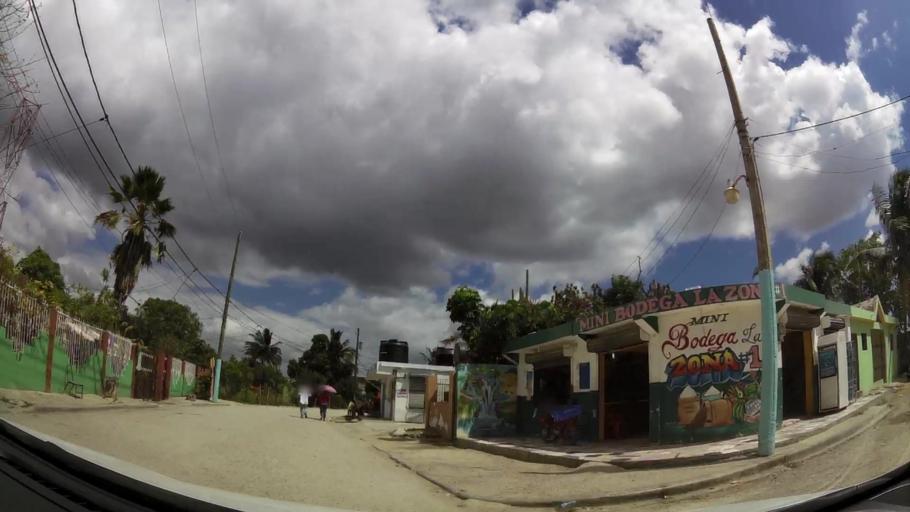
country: DO
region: Santo Domingo
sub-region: Santo Domingo
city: Boca Chica
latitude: 18.4524
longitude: -69.6598
